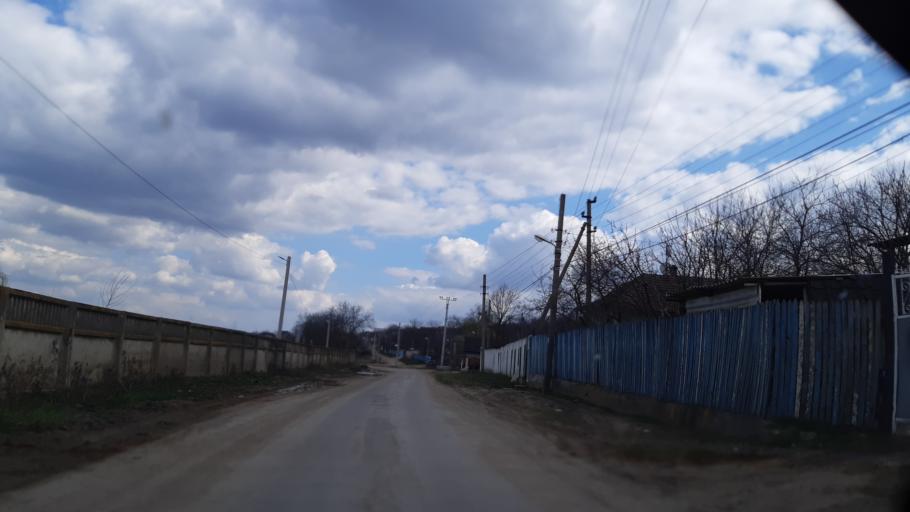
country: MD
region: Laloveni
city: Ialoveni
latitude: 46.8764
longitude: 28.7523
